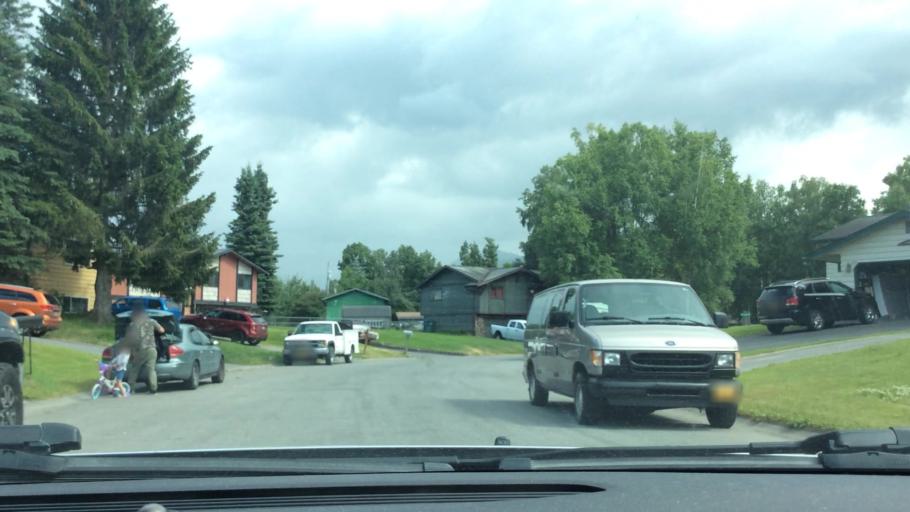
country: US
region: Alaska
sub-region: Anchorage Municipality
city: Elmendorf Air Force Base
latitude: 61.2218
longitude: -149.7539
